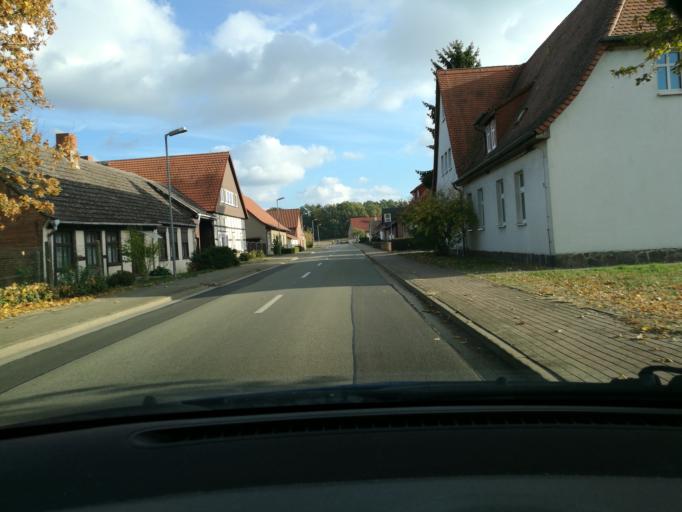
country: DE
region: Saxony-Anhalt
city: Luftkurort Arendsee
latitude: 52.8915
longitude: 11.4421
